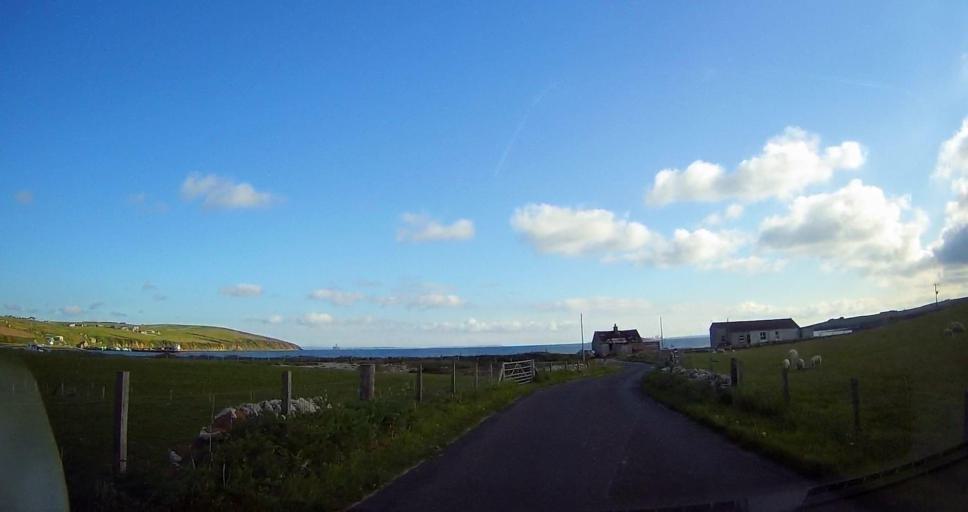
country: GB
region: Scotland
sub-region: Orkney Islands
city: Orkney
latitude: 58.9641
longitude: -2.9781
